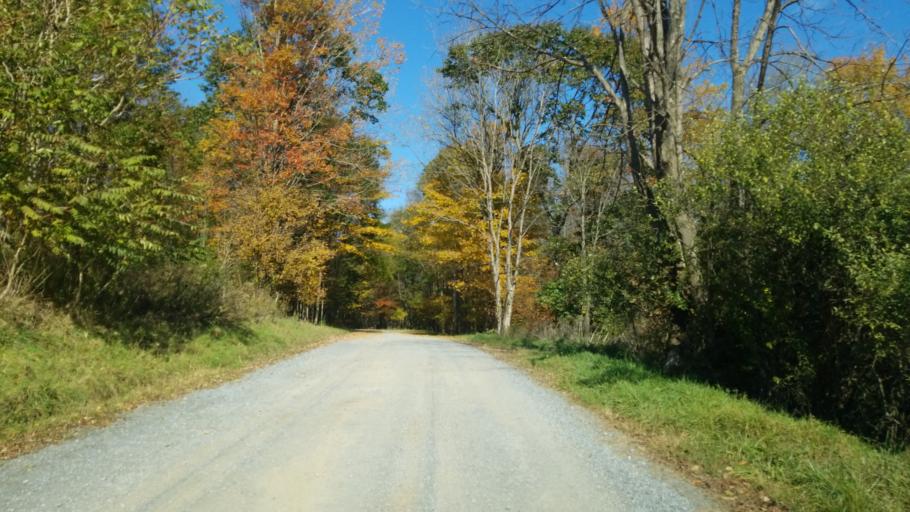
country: US
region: Pennsylvania
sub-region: Jefferson County
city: Falls Creek
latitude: 41.1870
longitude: -78.7822
